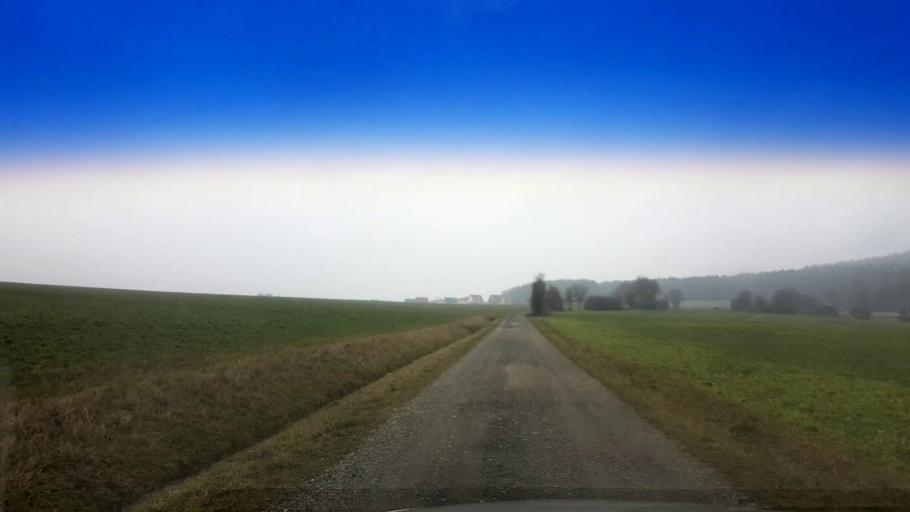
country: DE
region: Bavaria
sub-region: Upper Franconia
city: Litzendorf
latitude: 49.9176
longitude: 11.0137
